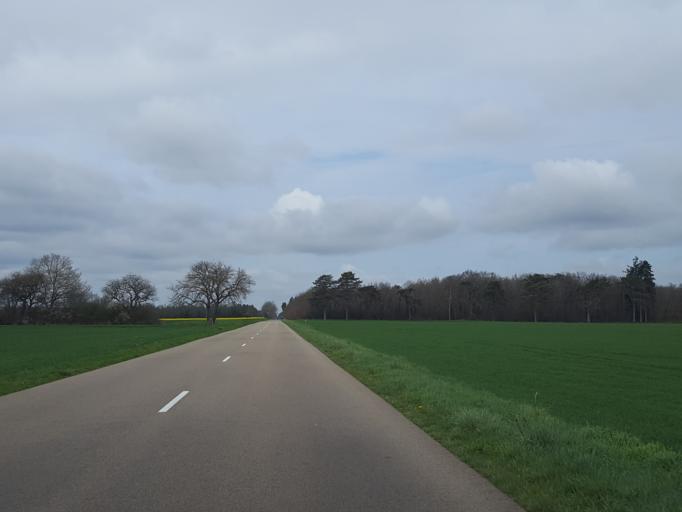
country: FR
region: Centre
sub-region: Departement du Loiret
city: Sainte-Genevieve-des-Bois
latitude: 47.8289
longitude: 2.7964
